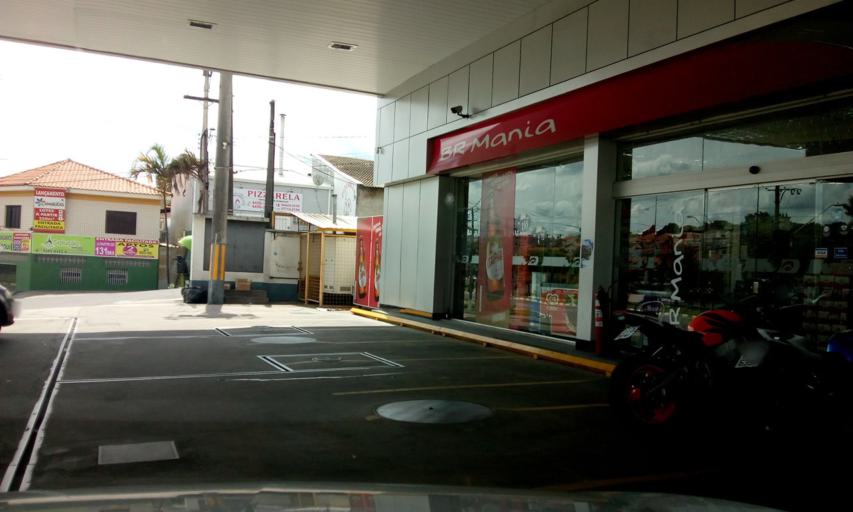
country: BR
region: Sao Paulo
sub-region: Itupeva
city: Itupeva
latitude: -23.1568
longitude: -47.0403
